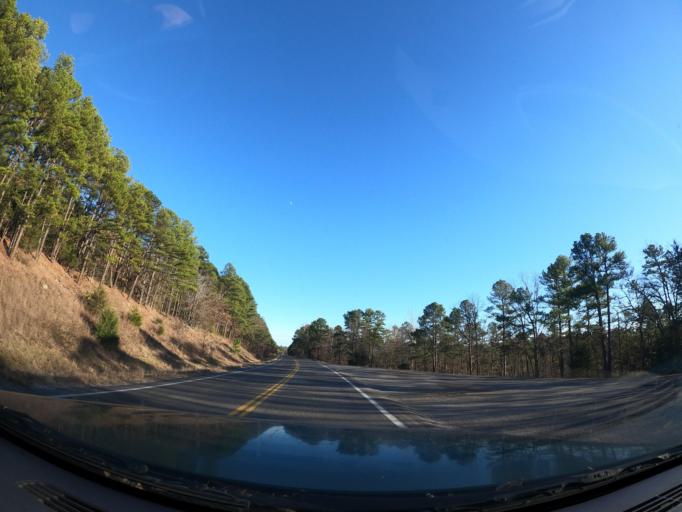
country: US
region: Oklahoma
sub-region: Latimer County
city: Wilburton
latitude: 34.9612
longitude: -95.3544
